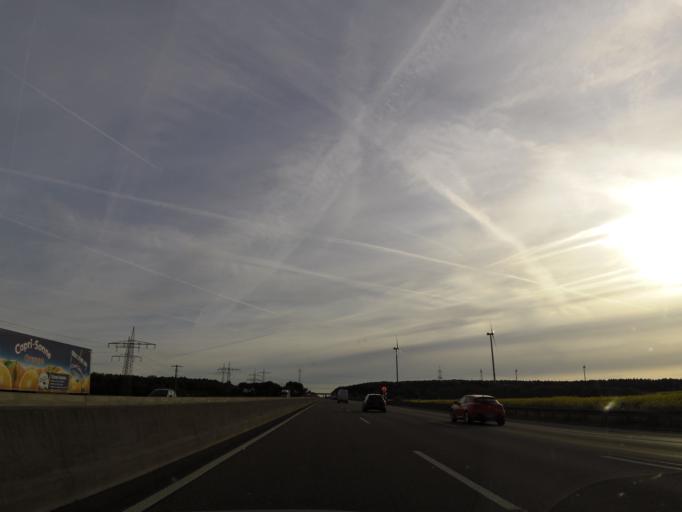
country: DE
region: Hesse
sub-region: Regierungsbezirk Kassel
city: Fuldatal
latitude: 51.3266
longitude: 9.5741
